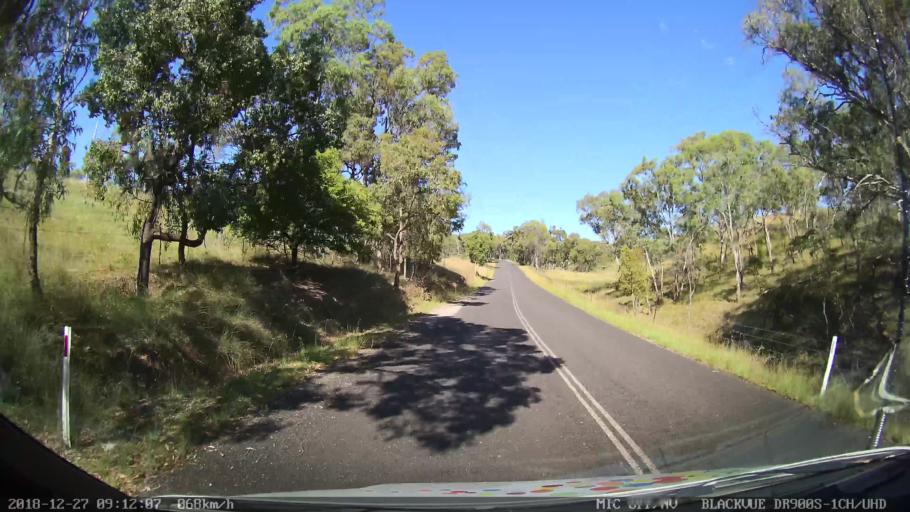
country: AU
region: New South Wales
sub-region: Lithgow
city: Portland
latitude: -33.1388
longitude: 150.1080
